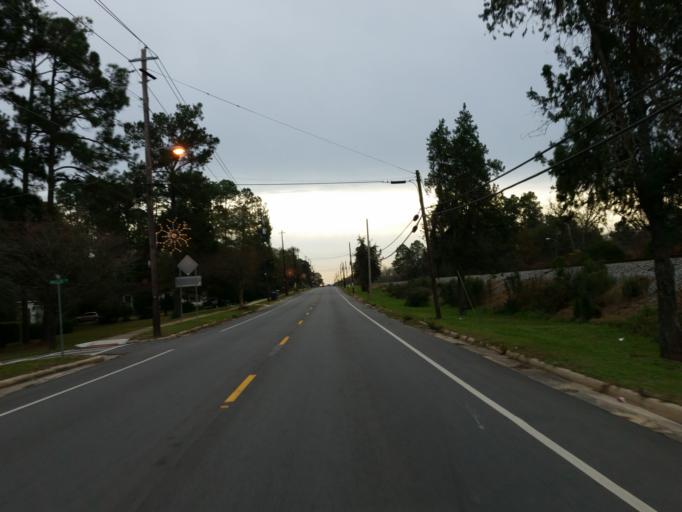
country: US
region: Georgia
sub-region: Turner County
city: Ashburn
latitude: 31.7000
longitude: -83.6505
